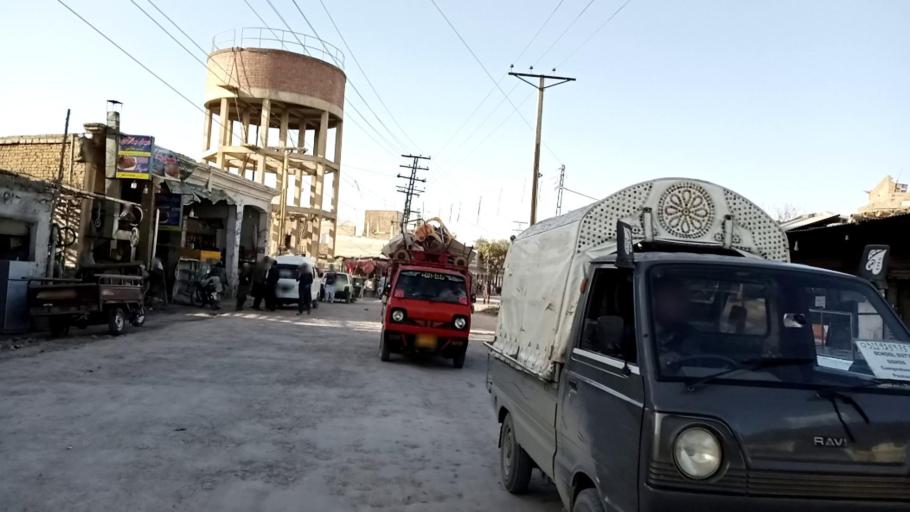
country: PK
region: Khyber Pakhtunkhwa
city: Peshawar
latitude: 34.0570
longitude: 71.5406
